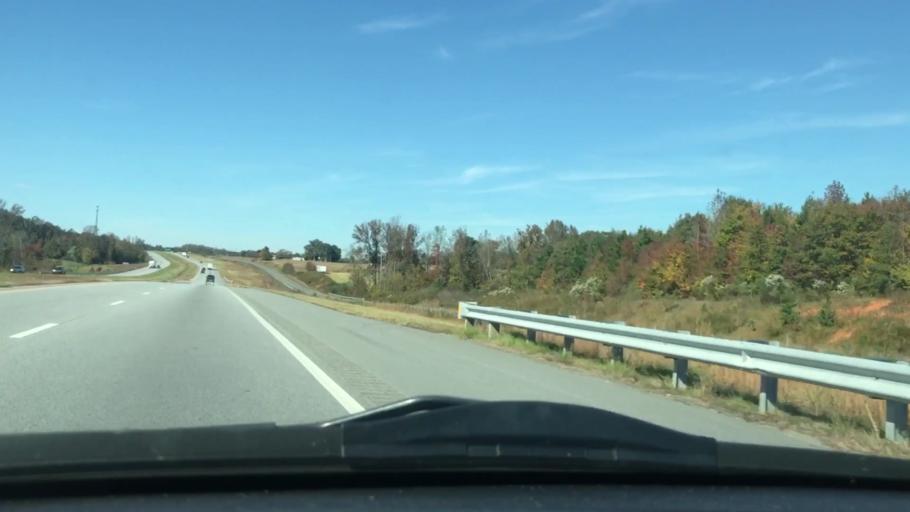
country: US
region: North Carolina
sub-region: Randolph County
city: Randleman
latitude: 35.8619
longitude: -79.8867
